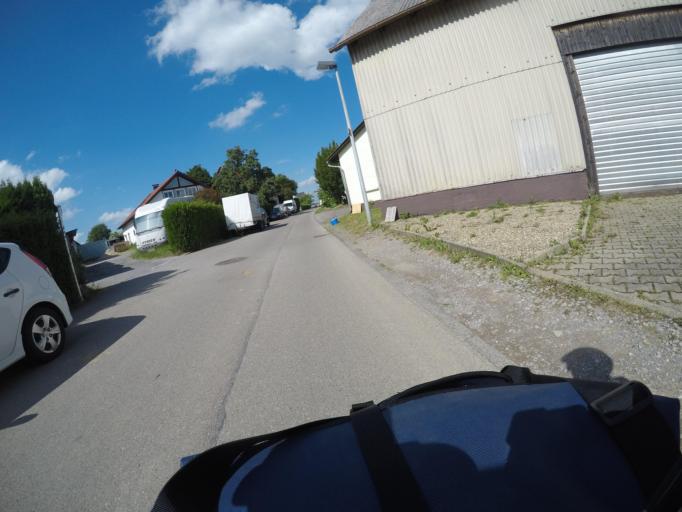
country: DE
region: Baden-Wuerttemberg
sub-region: Regierungsbezirk Stuttgart
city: Herrenberg
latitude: 48.6147
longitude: 8.8428
